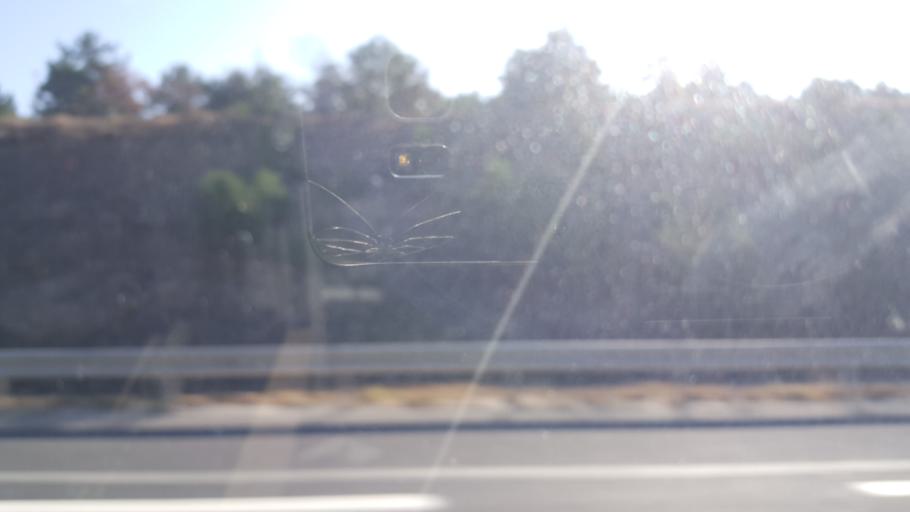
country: TR
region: Ankara
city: Mamak
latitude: 39.9167
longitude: 33.0038
